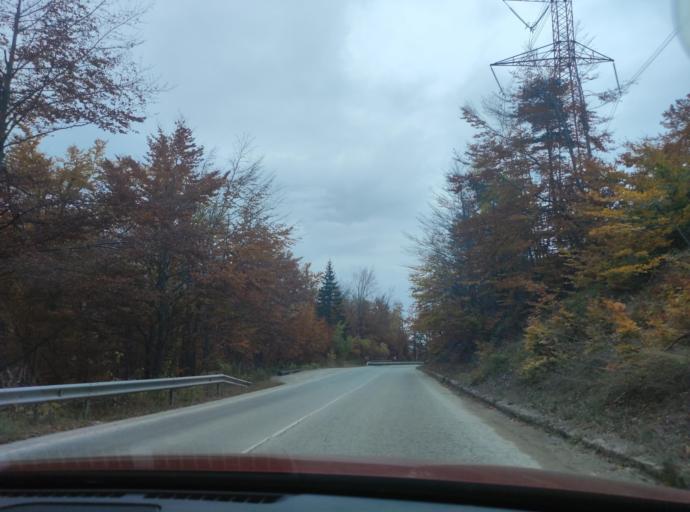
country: BG
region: Montana
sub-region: Obshtina Berkovitsa
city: Berkovitsa
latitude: 43.1302
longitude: 23.1347
